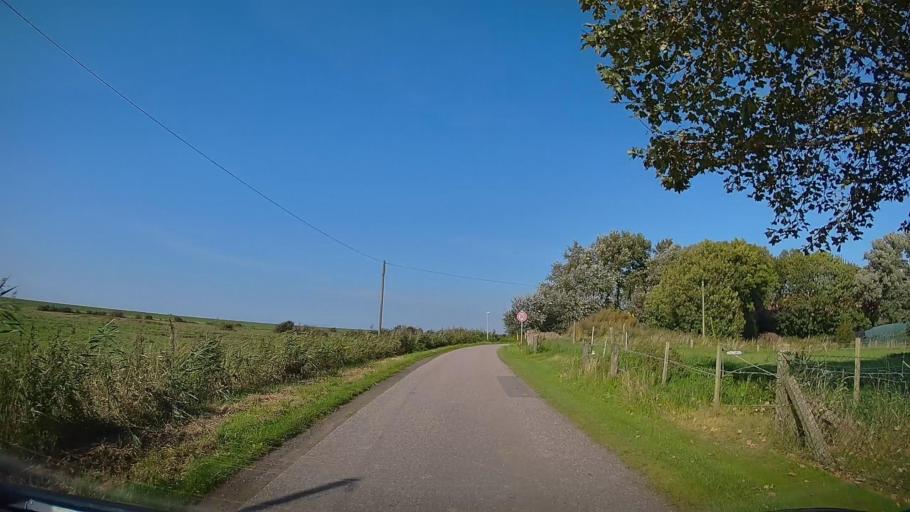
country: DE
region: Lower Saxony
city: Misselwarden
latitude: 53.6953
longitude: 8.4924
